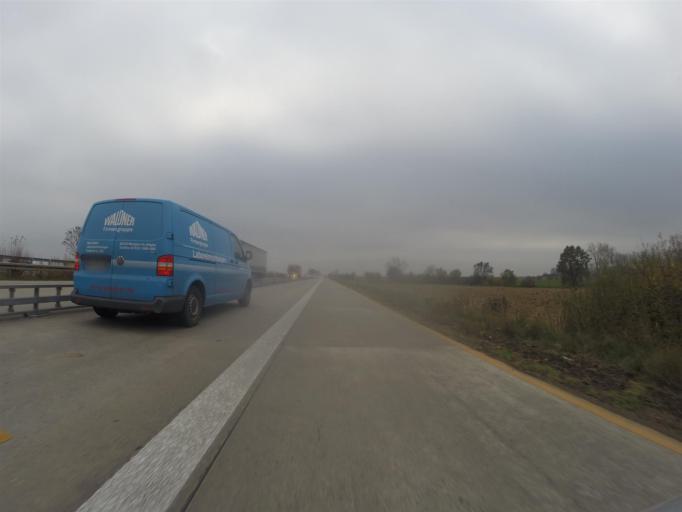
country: DE
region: Saxony-Anhalt
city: Osterfeld
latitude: 51.0790
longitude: 11.9553
